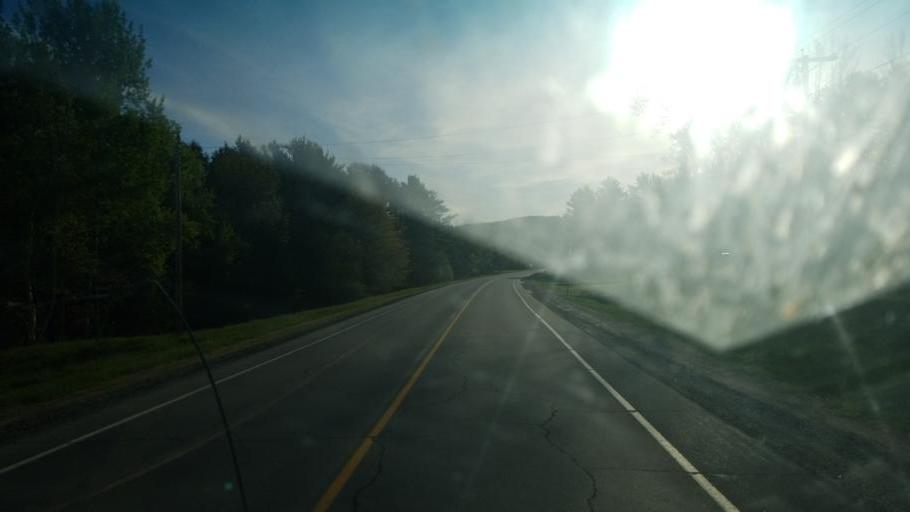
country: US
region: New Hampshire
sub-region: Grafton County
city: Littleton
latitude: 44.3209
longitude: -71.8153
